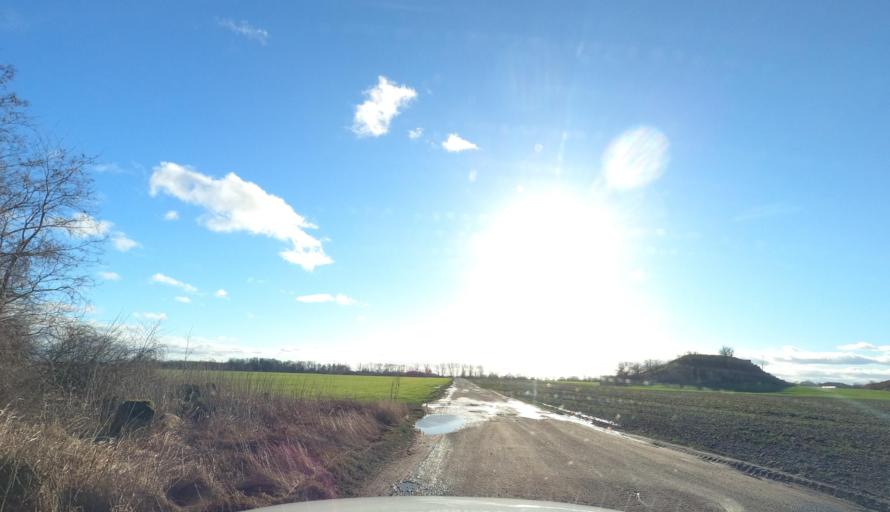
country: PL
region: West Pomeranian Voivodeship
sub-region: Powiat pyrzycki
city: Warnice
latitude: 53.2890
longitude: 14.9923
